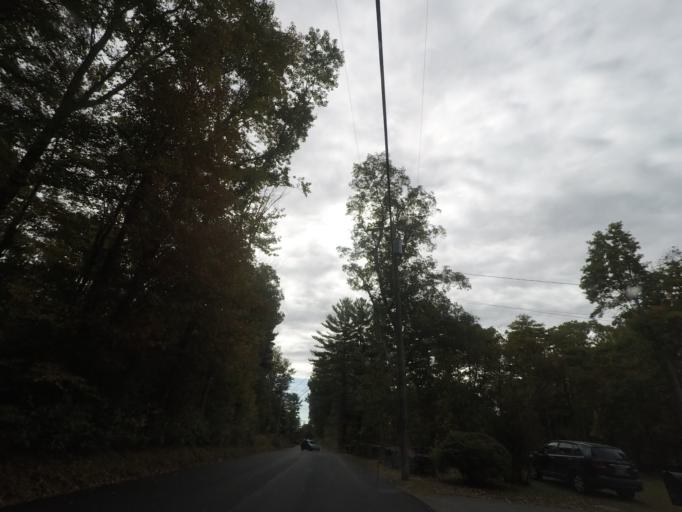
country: US
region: Connecticut
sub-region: Windham County
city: Thompson
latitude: 41.9716
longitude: -71.8376
